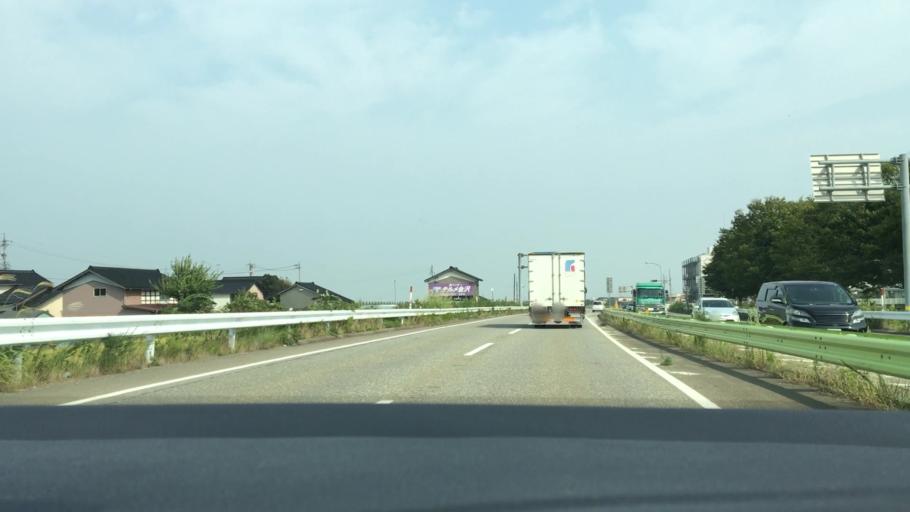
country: JP
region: Ishikawa
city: Matsuto
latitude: 36.5065
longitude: 136.5953
